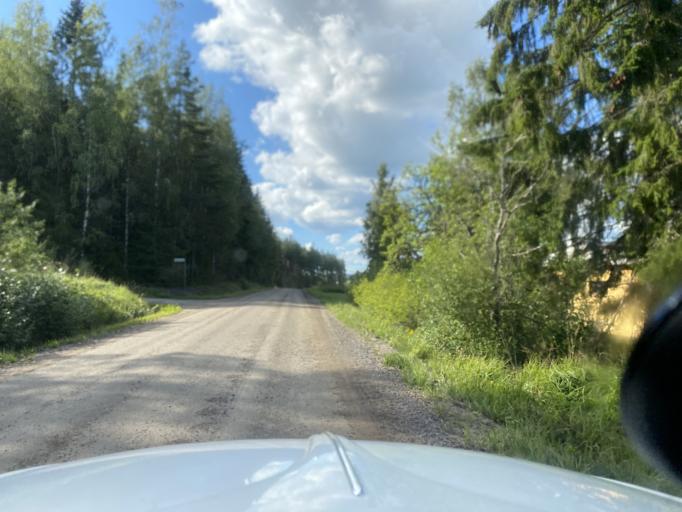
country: FI
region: Pirkanmaa
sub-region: Lounais-Pirkanmaa
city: Punkalaidun
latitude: 61.1237
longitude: 23.2617
